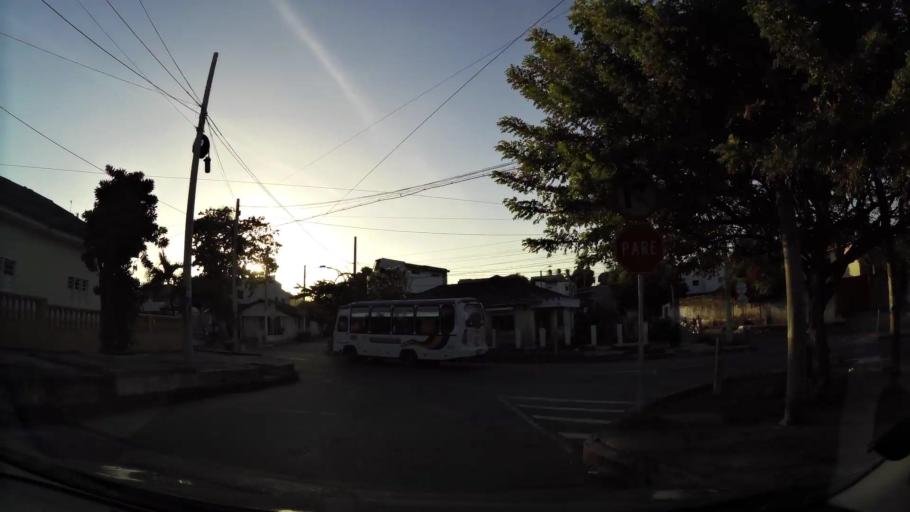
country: CO
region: Atlantico
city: Barranquilla
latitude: 10.9791
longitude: -74.7958
